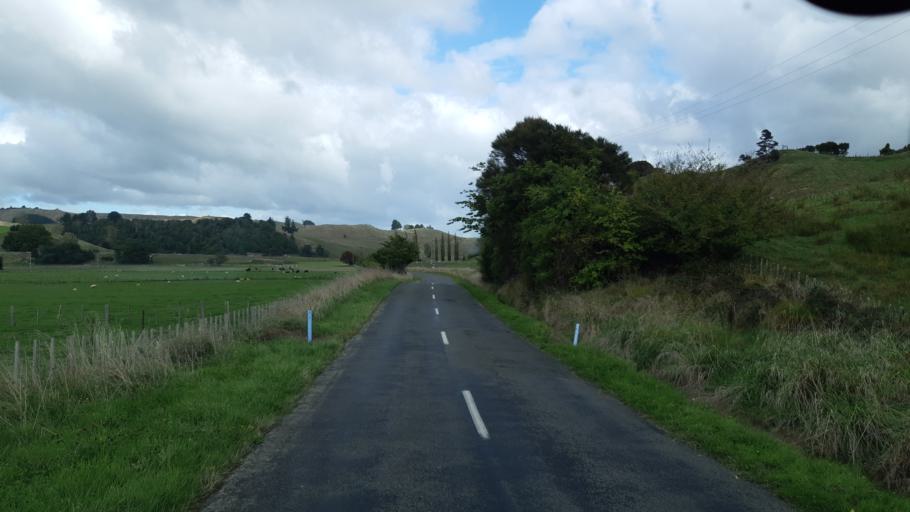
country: NZ
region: Manawatu-Wanganui
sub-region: Rangitikei District
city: Bulls
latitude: -39.9161
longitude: 175.5927
